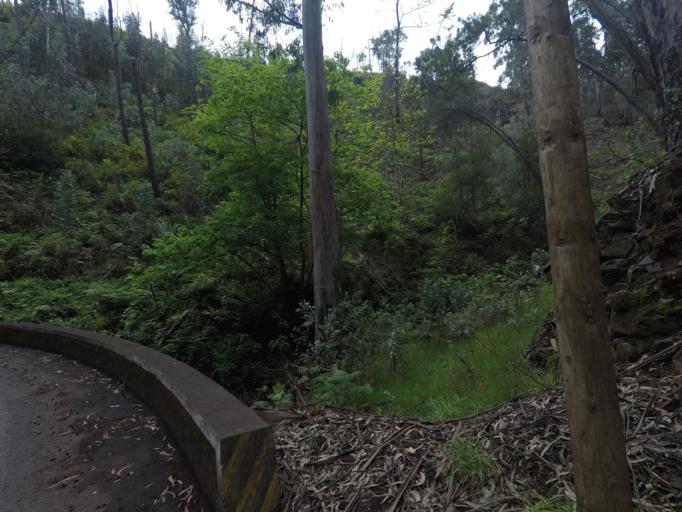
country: PT
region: Madeira
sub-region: Calheta
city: Estreito da Calheta
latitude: 32.7561
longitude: -17.1959
